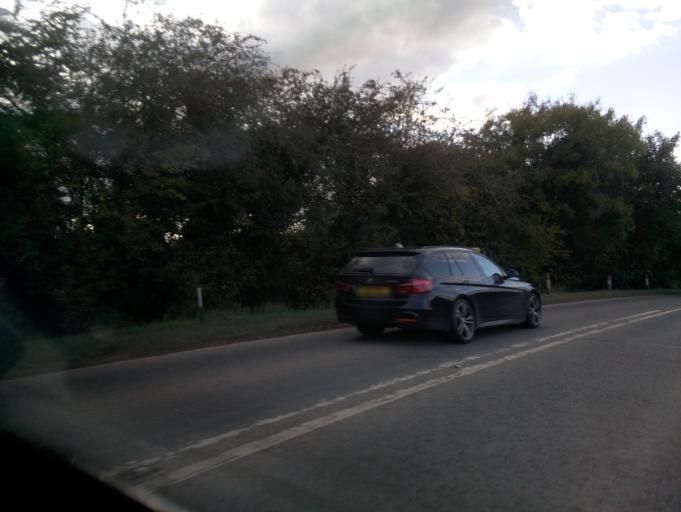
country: GB
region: England
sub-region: Herefordshire
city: Ocle Pychard
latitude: 52.0623
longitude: -2.5435
